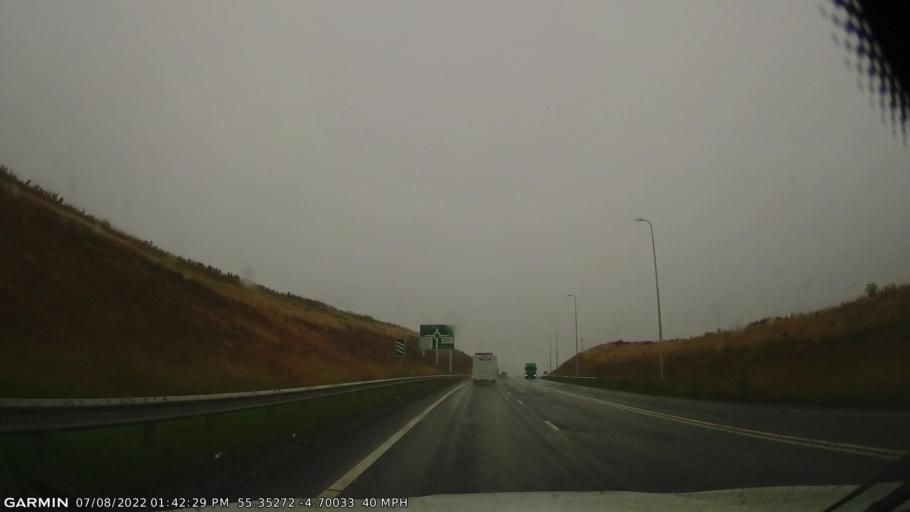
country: GB
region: Scotland
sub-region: South Ayrshire
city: Maybole
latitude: 55.3522
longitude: -4.7002
